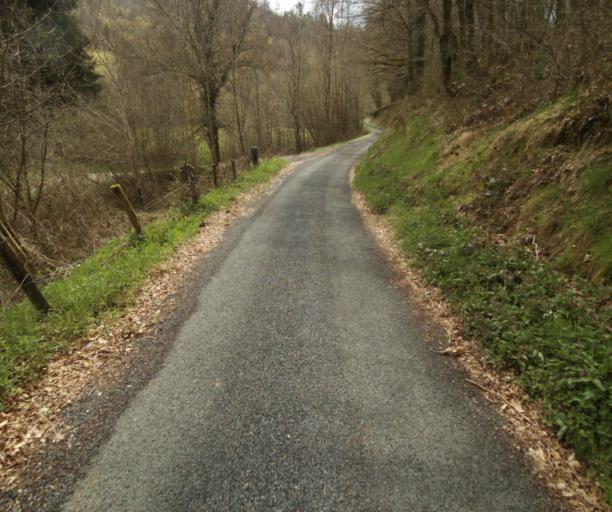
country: FR
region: Limousin
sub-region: Departement de la Correze
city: Tulle
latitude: 45.2749
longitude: 1.8018
